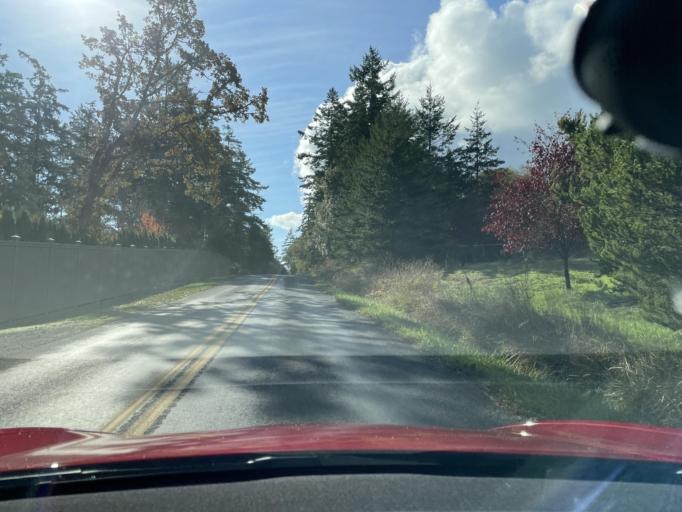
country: US
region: Washington
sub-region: San Juan County
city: Friday Harbor
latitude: 48.5095
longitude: -123.0231
